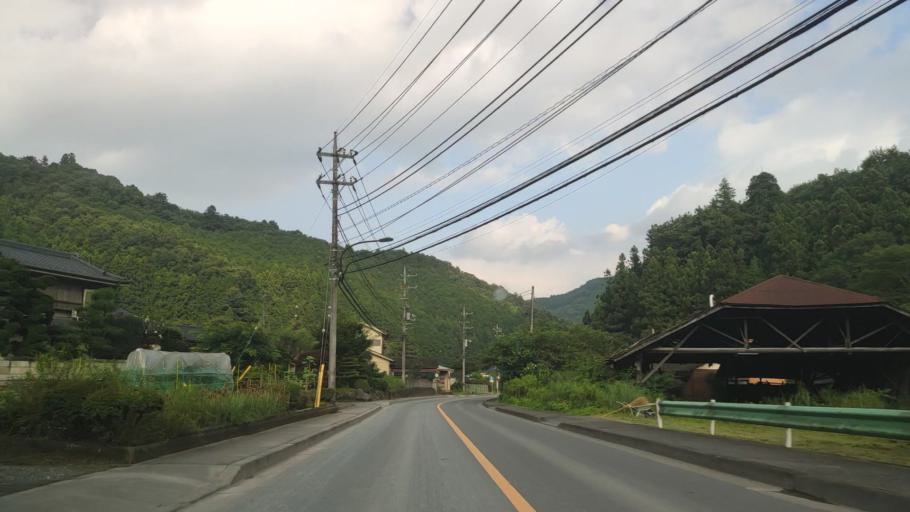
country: JP
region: Tokyo
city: Ome
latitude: 35.8255
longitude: 139.2451
